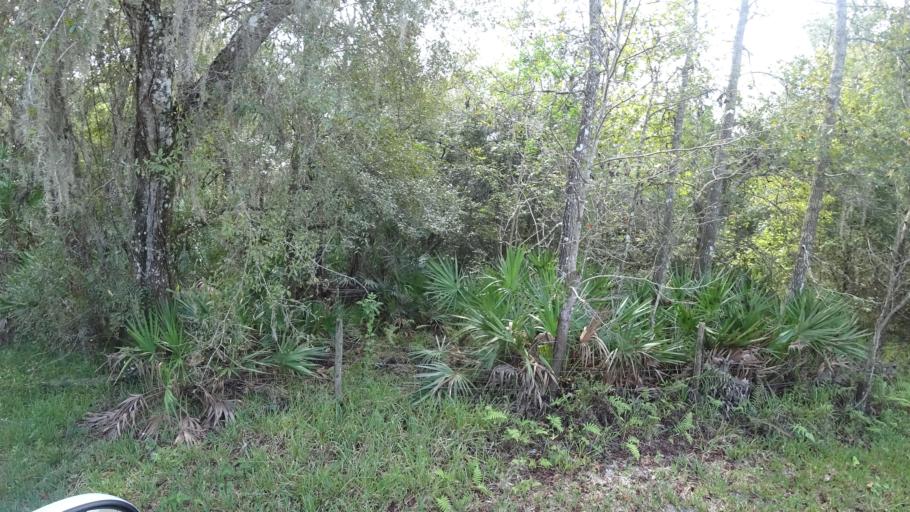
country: US
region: Florida
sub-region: Hillsborough County
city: Wimauma
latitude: 27.5907
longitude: -82.1825
